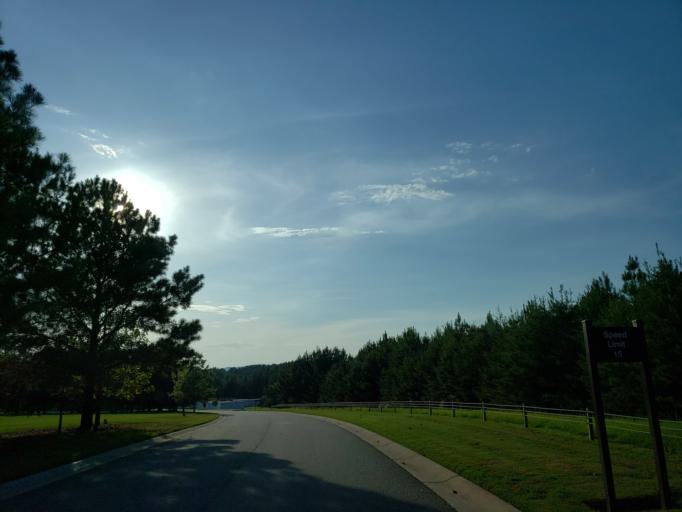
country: US
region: Georgia
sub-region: Cherokee County
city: Canton
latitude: 34.2368
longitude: -84.5804
